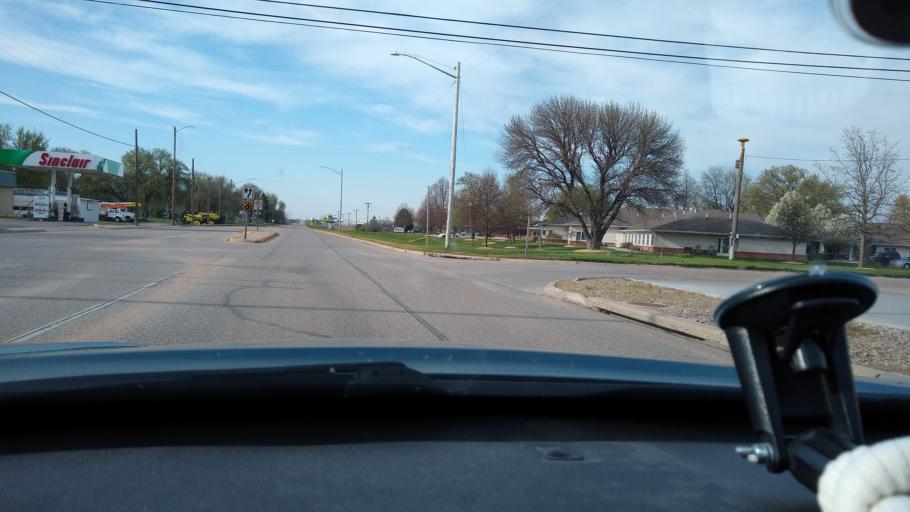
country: US
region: Nebraska
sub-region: Fillmore County
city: Geneva
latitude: 40.5295
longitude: -97.5958
